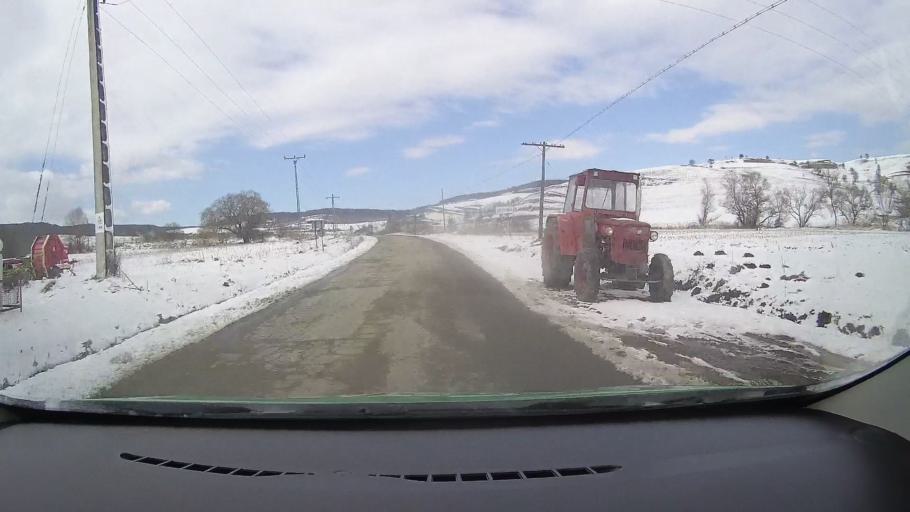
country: RO
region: Sibiu
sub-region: Comuna Altina
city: Altina
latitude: 45.9872
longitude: 24.4520
